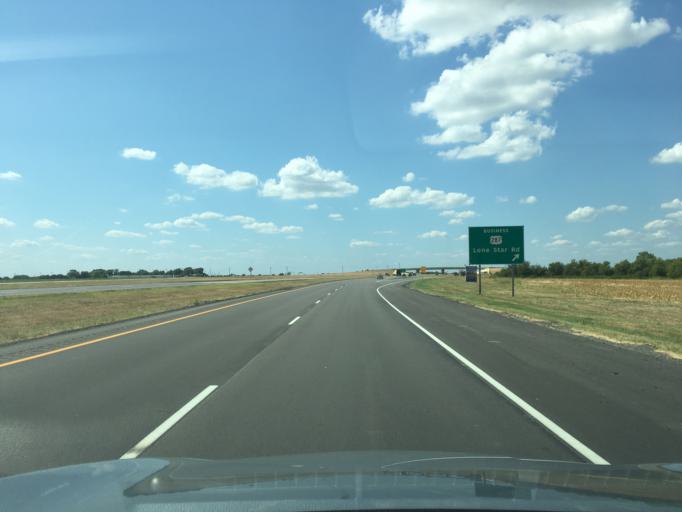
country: US
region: Texas
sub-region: Tarrant County
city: Mansfield
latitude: 32.5323
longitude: -97.0992
